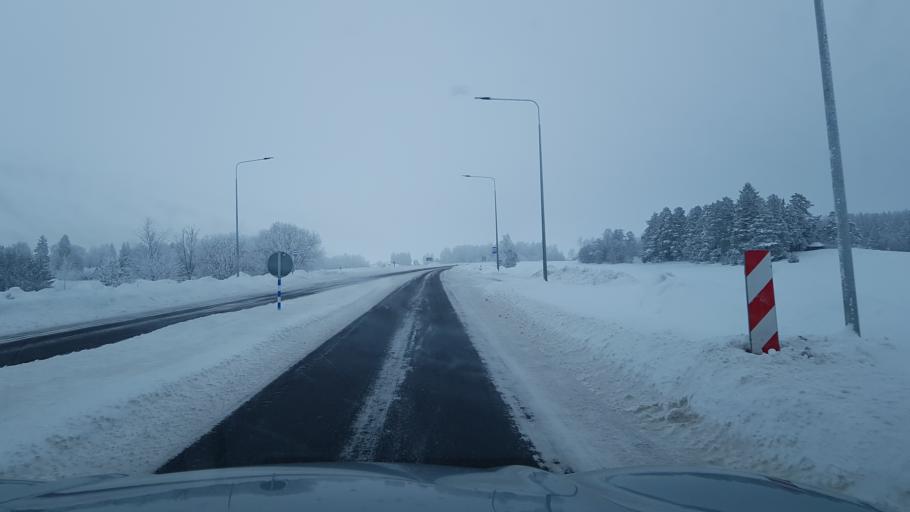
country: EE
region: Ida-Virumaa
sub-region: Johvi vald
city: Johvi
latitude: 59.2273
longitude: 27.3388
